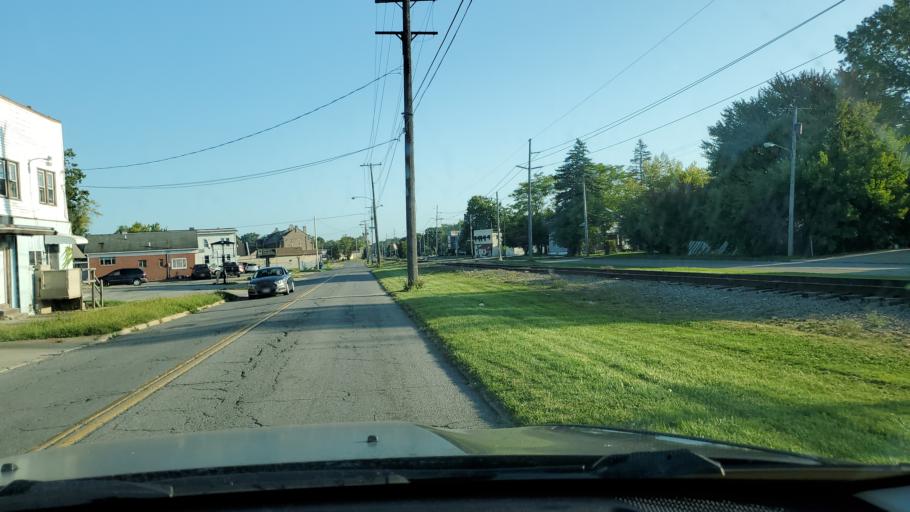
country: US
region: Ohio
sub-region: Mahoning County
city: Youngstown
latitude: 41.0626
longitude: -80.6575
